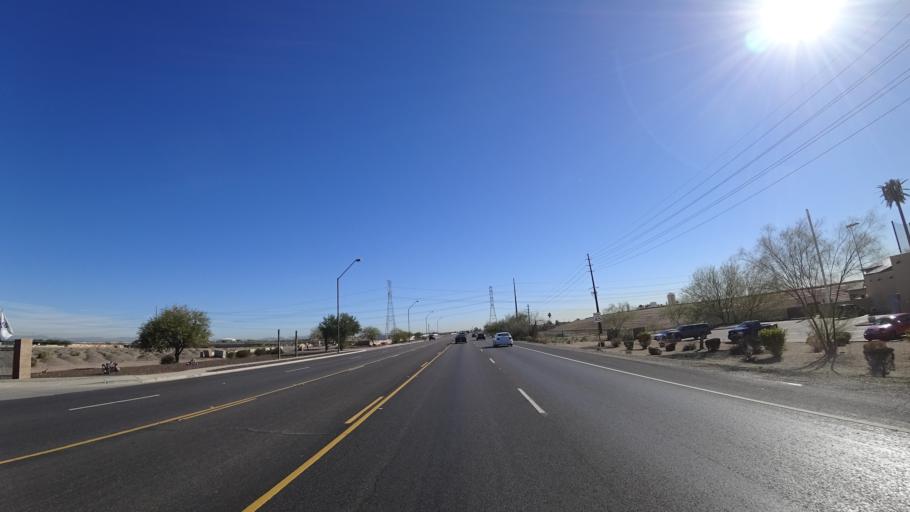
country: US
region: Arizona
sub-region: Maricopa County
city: Litchfield Park
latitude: 33.4932
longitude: -112.3223
